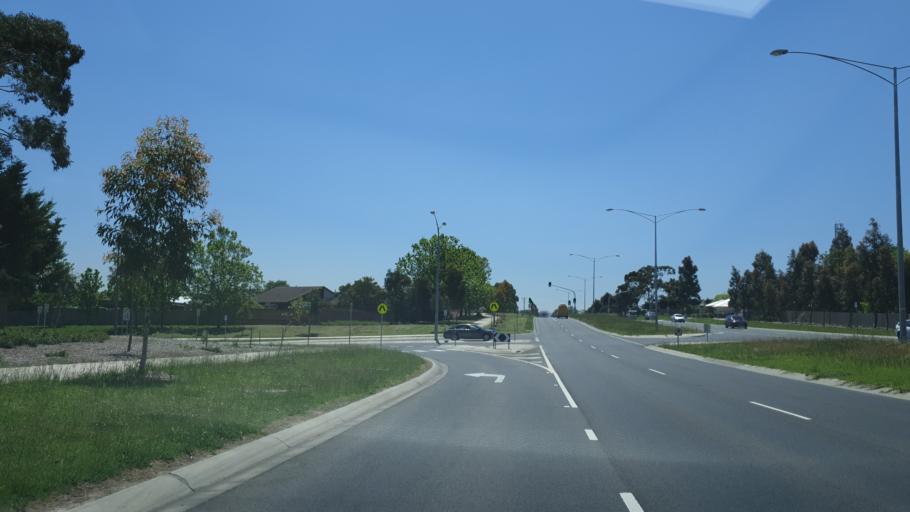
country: AU
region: Victoria
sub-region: Casey
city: Narre Warren South
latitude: -38.0593
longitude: 145.3001
